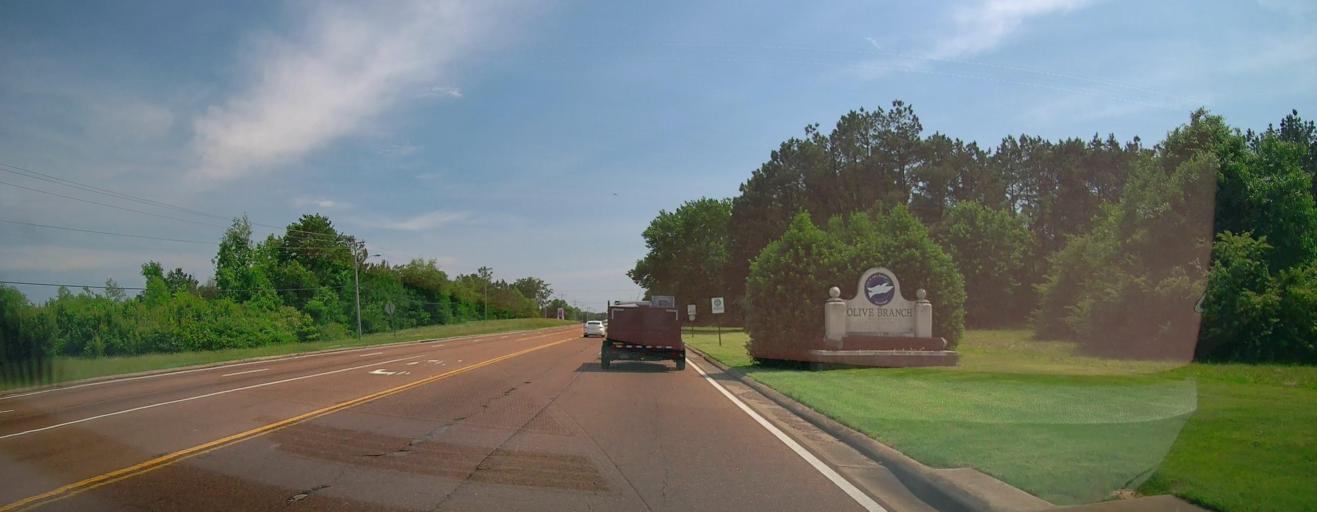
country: US
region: Mississippi
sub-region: De Soto County
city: Olive Branch
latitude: 34.9945
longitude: -89.8308
